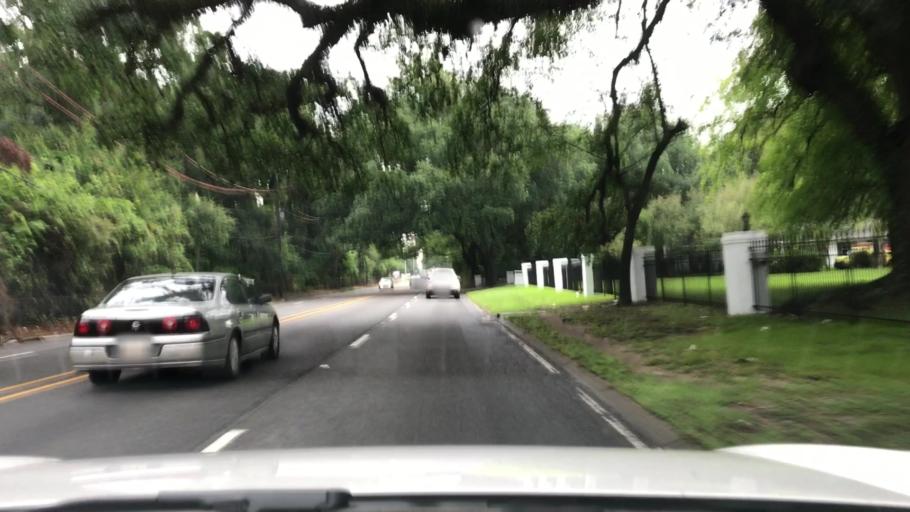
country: US
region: Louisiana
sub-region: East Baton Rouge Parish
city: Baton Rouge
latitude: 30.4563
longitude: -91.1392
